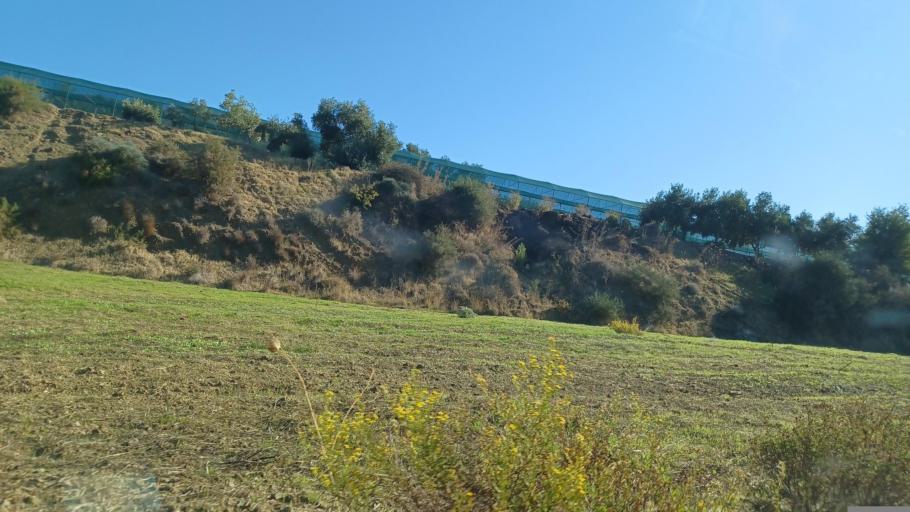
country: CY
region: Pafos
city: Polis
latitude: 35.0209
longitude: 32.4926
